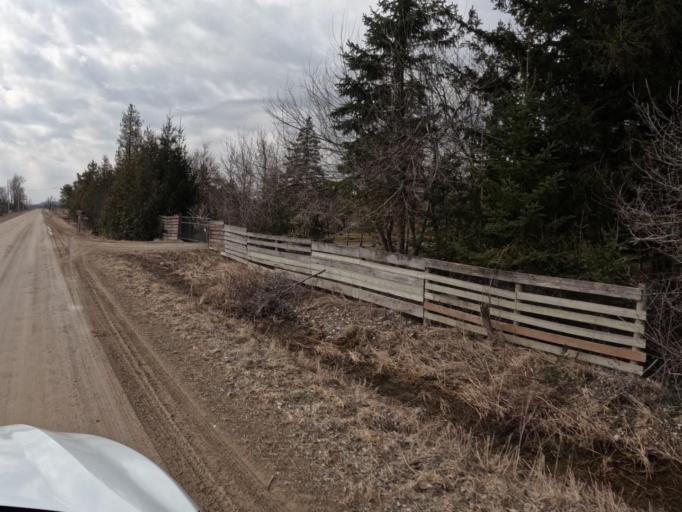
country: CA
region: Ontario
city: Orangeville
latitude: 43.9118
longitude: -80.2159
